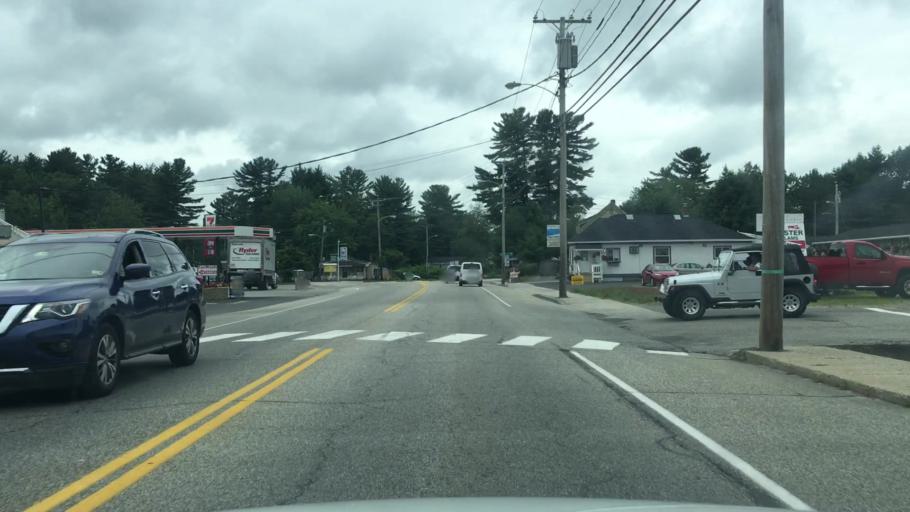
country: US
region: Maine
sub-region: York County
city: Old Orchard Beach
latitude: 43.5083
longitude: -70.4074
